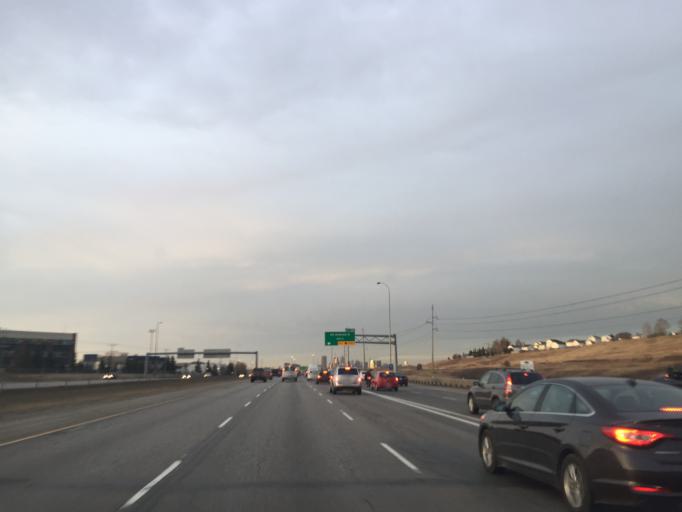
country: CA
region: Alberta
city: Calgary
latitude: 51.1213
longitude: -114.0463
